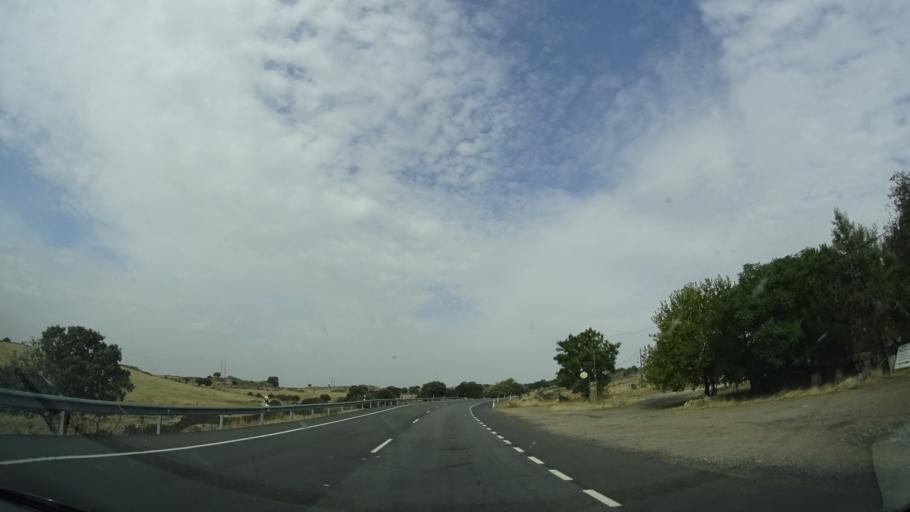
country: ES
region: Extremadura
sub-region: Provincia de Caceres
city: Trujillo
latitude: 39.4175
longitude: -5.8932
